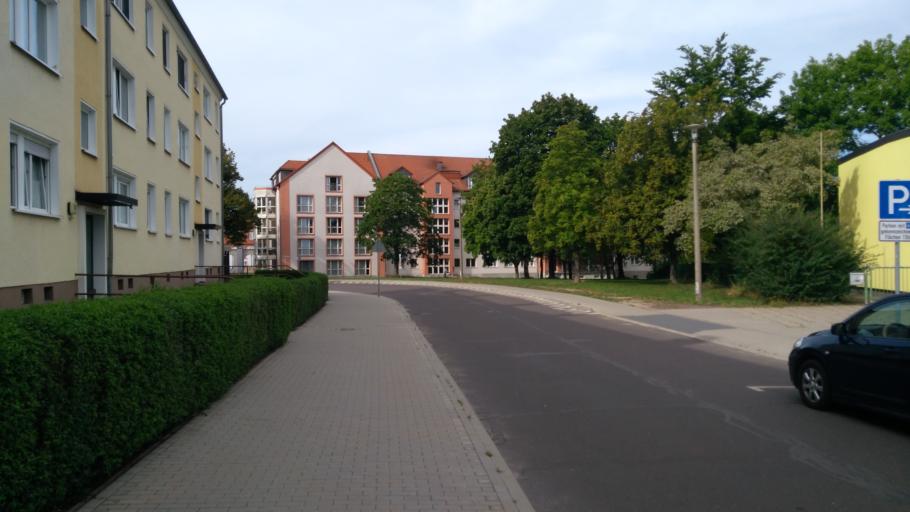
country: DE
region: Saxony-Anhalt
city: Zerbst
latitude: 51.9689
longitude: 12.0815
